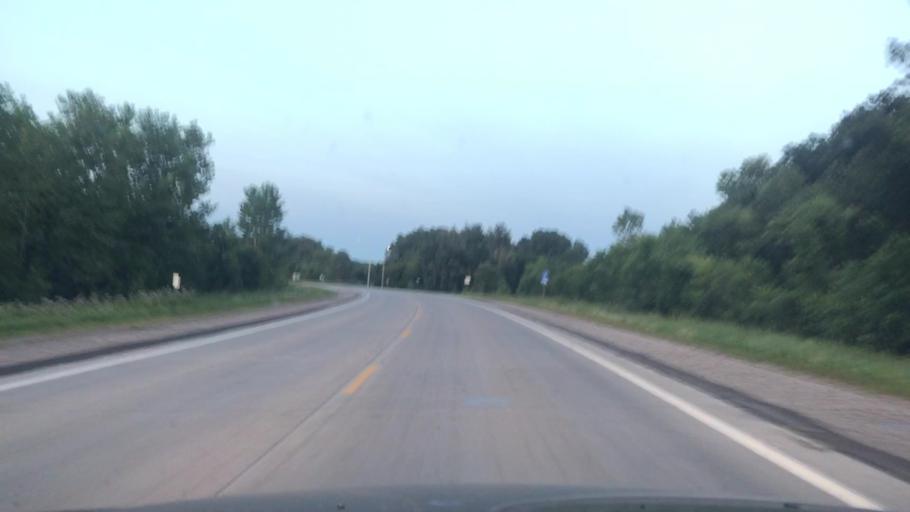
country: US
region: Minnesota
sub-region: Redwood County
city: Redwood Falls
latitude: 44.5401
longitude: -95.0091
